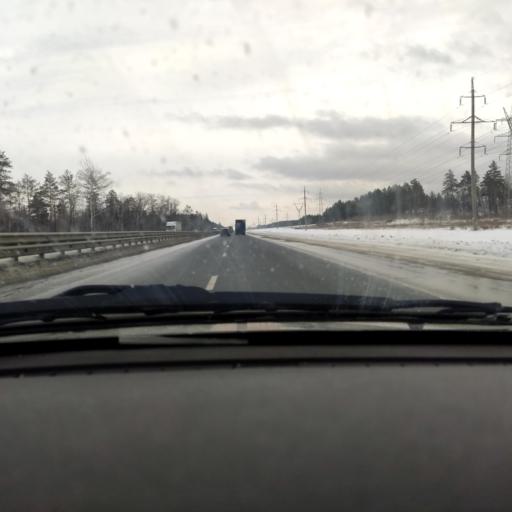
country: RU
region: Samara
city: Povolzhskiy
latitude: 53.5155
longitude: 49.7055
